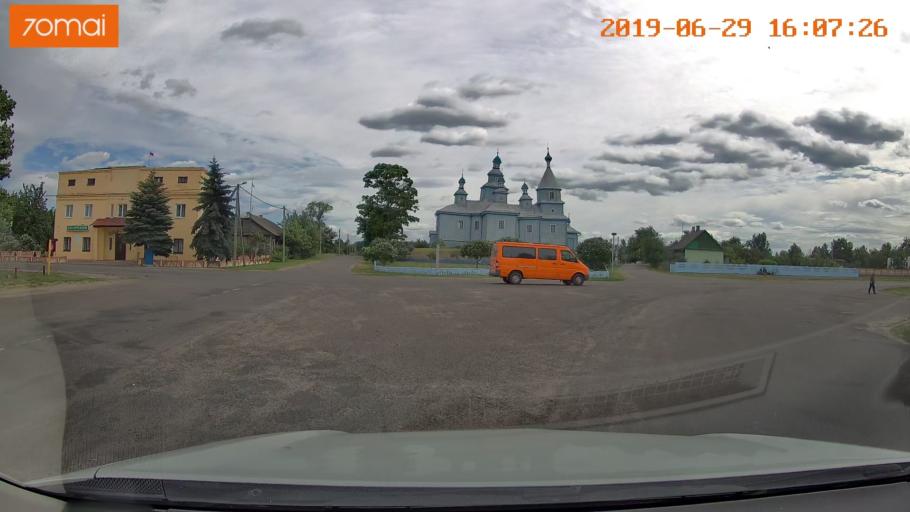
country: BY
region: Brest
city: Luninyets
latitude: 52.2062
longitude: 27.0101
